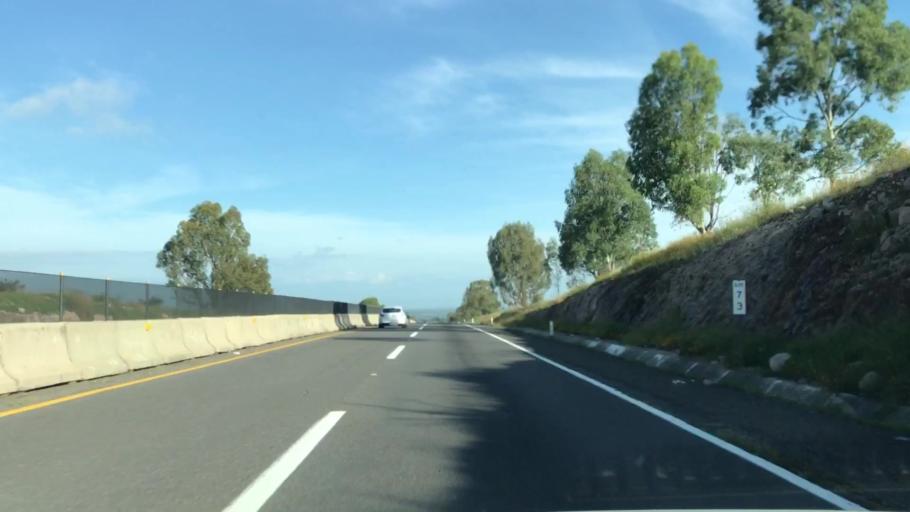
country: MX
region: Jalisco
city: Encarnacion de Diaz
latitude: 21.3856
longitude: -102.1417
